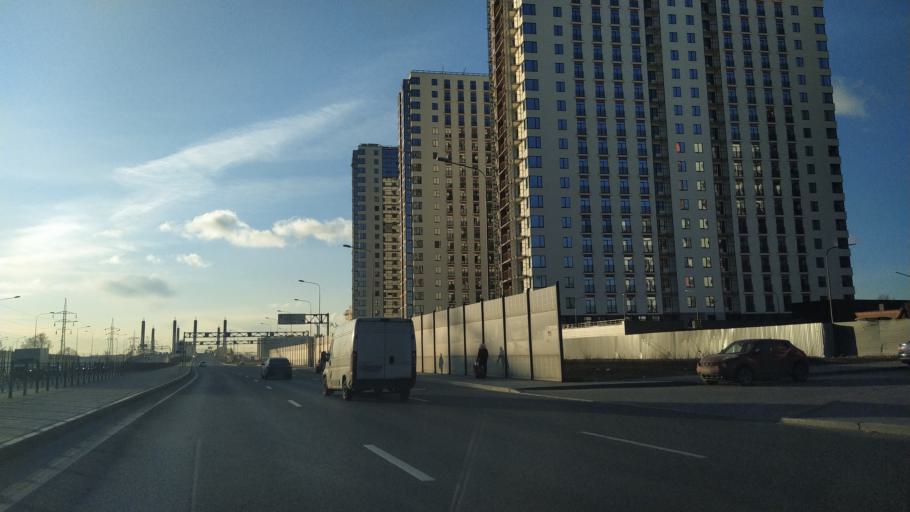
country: RU
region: St.-Petersburg
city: Kupchino
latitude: 59.8306
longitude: 30.3327
